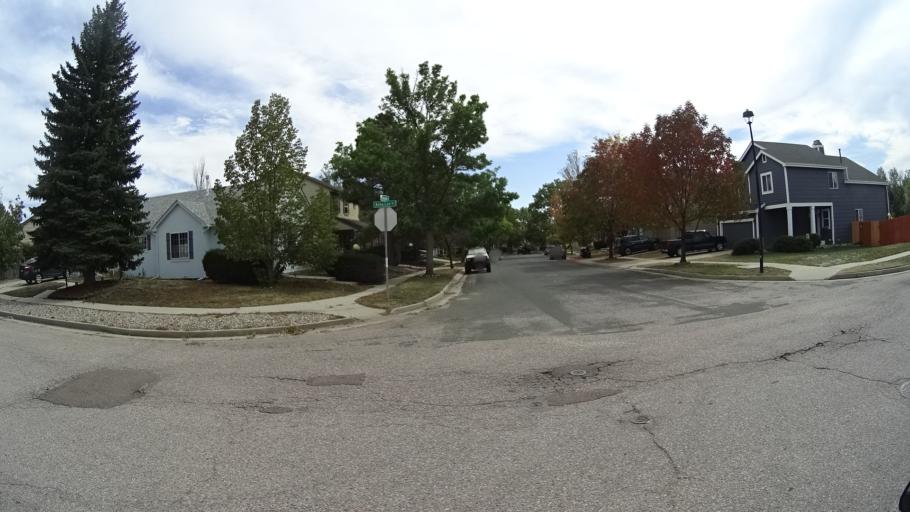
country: US
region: Colorado
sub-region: El Paso County
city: Cimarron Hills
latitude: 38.9062
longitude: -104.7067
